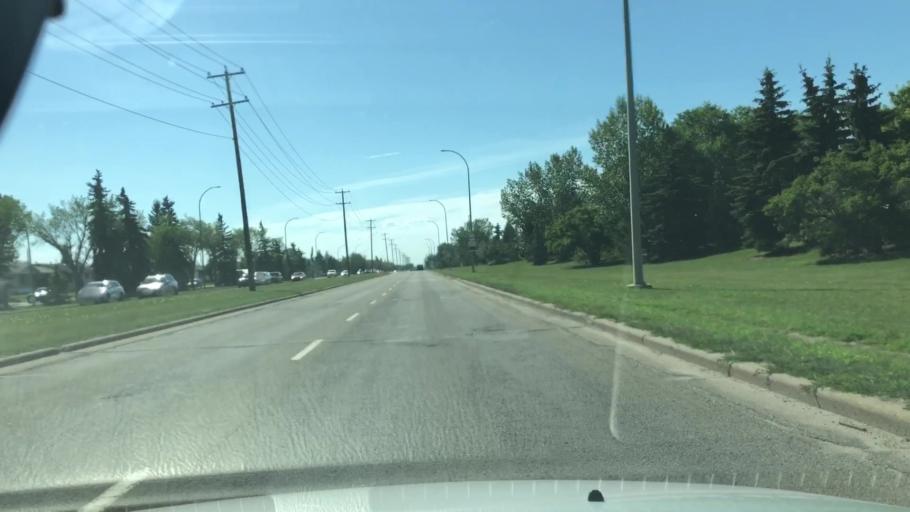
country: CA
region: Alberta
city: Edmonton
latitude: 53.5997
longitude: -113.5224
